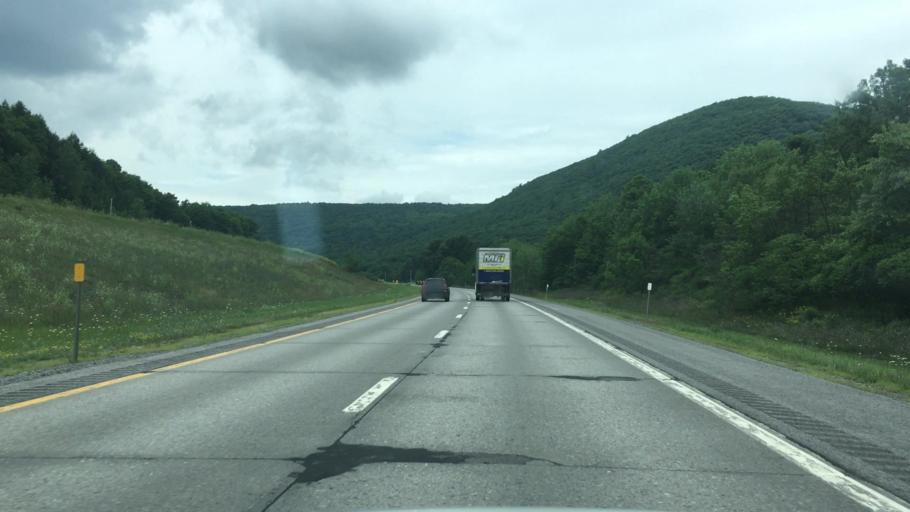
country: US
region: New York
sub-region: Otsego County
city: Worcester
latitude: 42.6502
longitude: -74.6277
